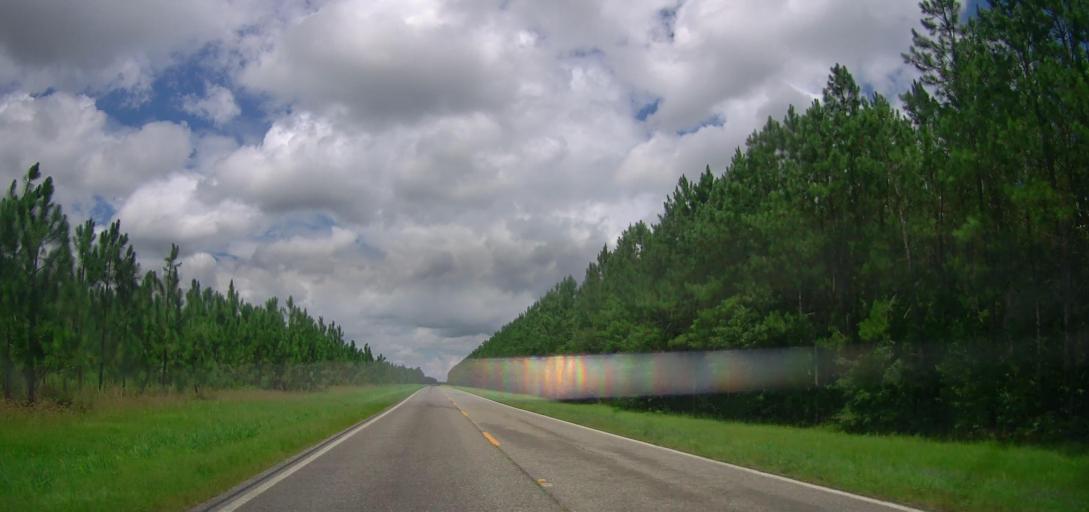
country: US
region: Georgia
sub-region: Wilcox County
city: Rochelle
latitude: 31.8652
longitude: -83.5584
